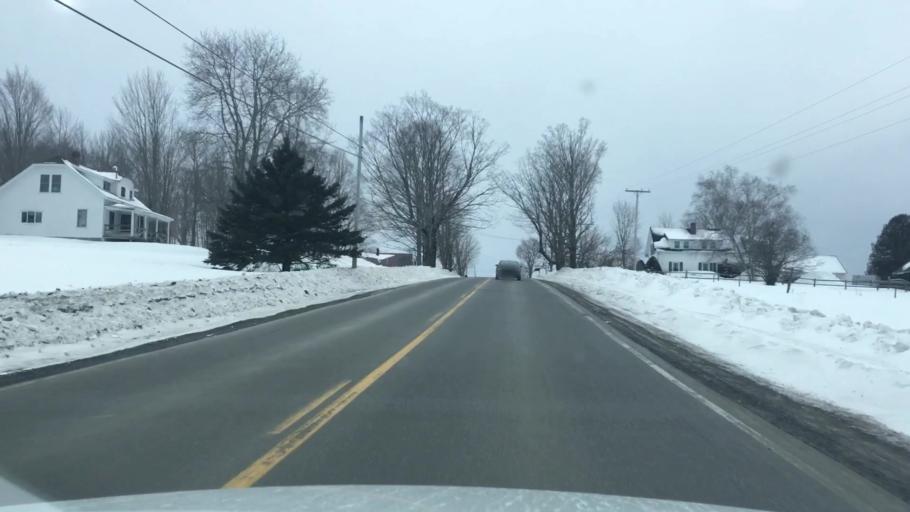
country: US
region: Maine
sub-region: Penobscot County
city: Charleston
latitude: 44.9960
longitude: -69.0418
